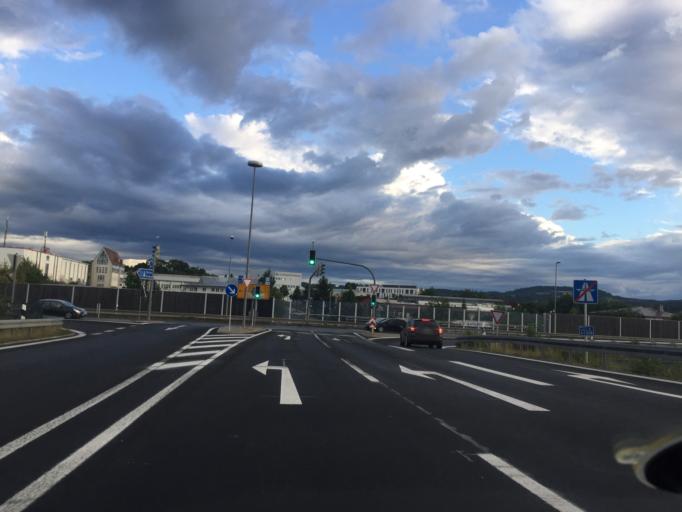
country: DE
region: Bavaria
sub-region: Upper Franconia
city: Bayreuth
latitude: 49.9291
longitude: 11.6006
